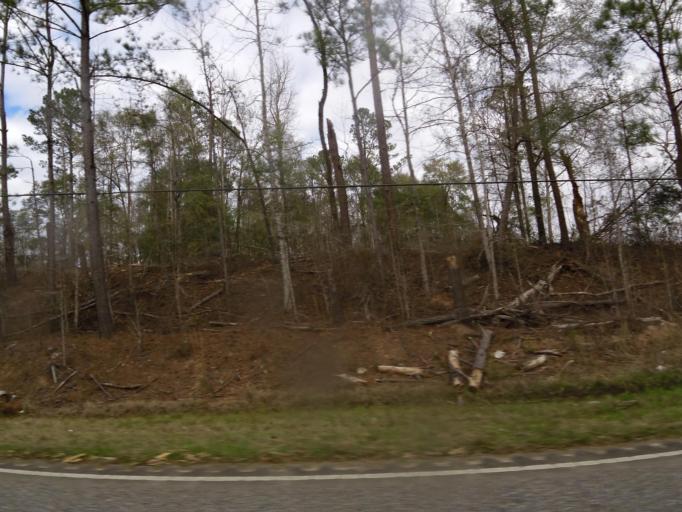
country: US
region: Alabama
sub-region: Barbour County
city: Eufaula
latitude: 31.9501
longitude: -85.1965
